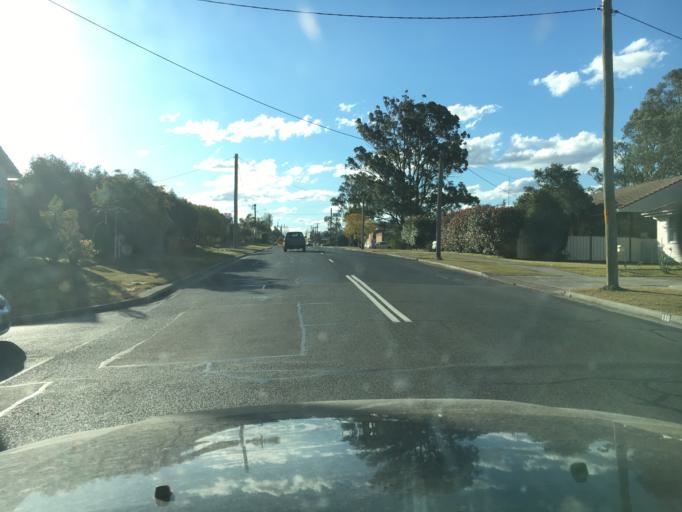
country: AU
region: New South Wales
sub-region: Maitland Municipality
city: East Maitland
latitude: -32.7607
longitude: 151.5864
